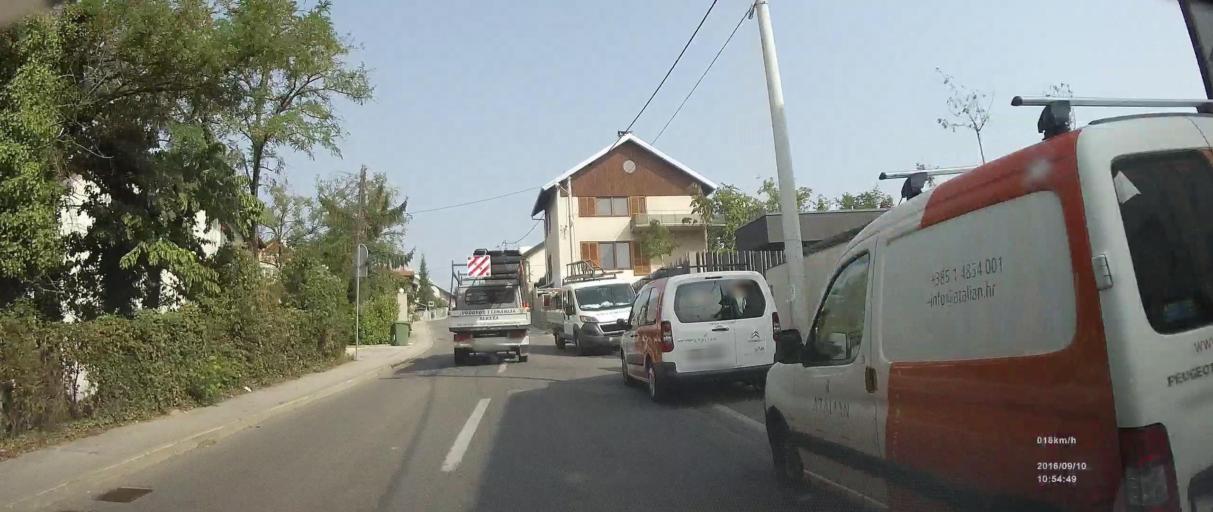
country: HR
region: Grad Zagreb
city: Zagreb
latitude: 45.8281
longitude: 15.9384
